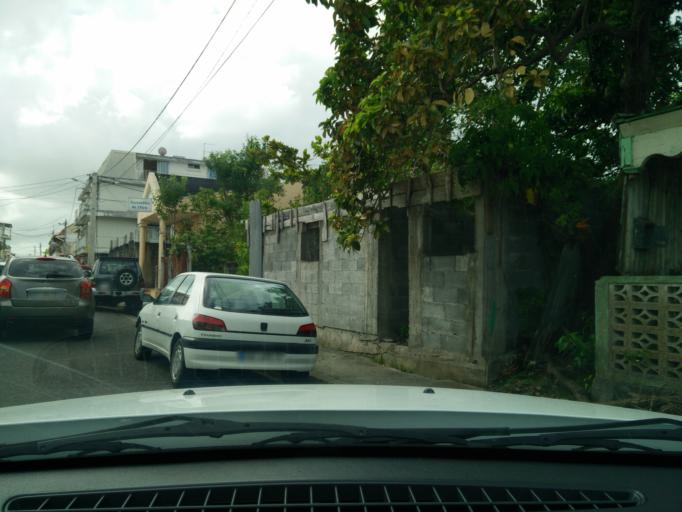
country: GP
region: Guadeloupe
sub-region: Guadeloupe
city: Petit-Canal
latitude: 16.3322
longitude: -61.4593
